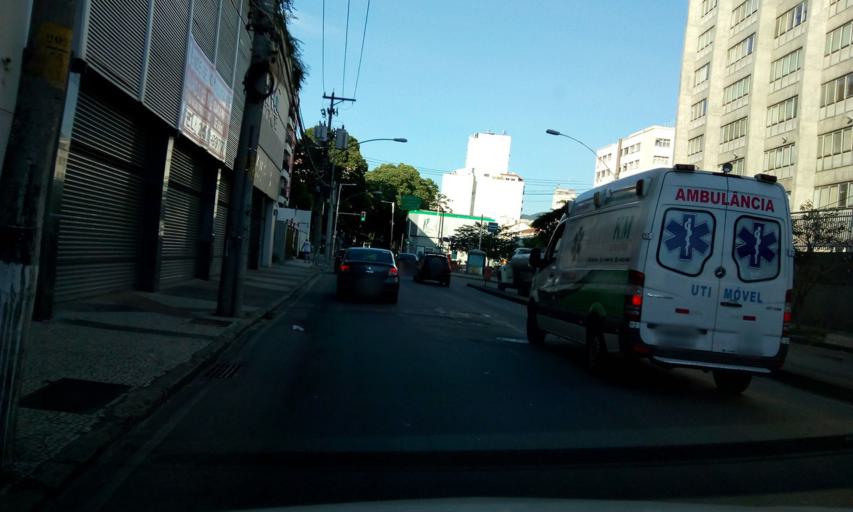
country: BR
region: Rio de Janeiro
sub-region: Rio De Janeiro
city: Rio de Janeiro
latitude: -22.9560
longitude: -43.1909
